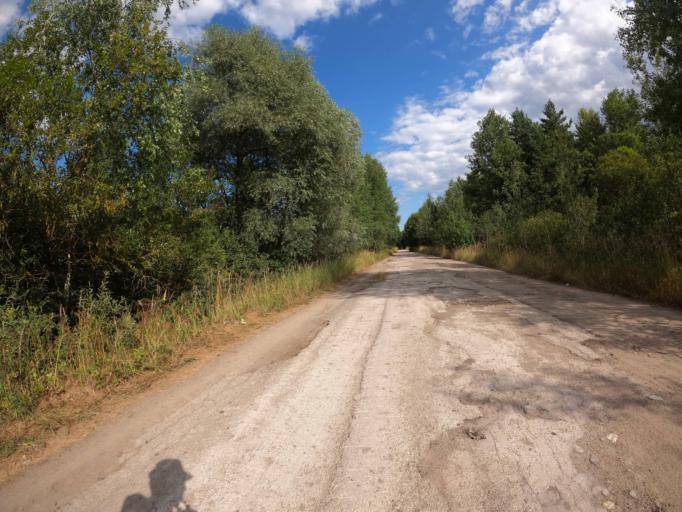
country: RU
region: Moskovskaya
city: Konobeyevo
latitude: 55.3848
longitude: 38.7007
